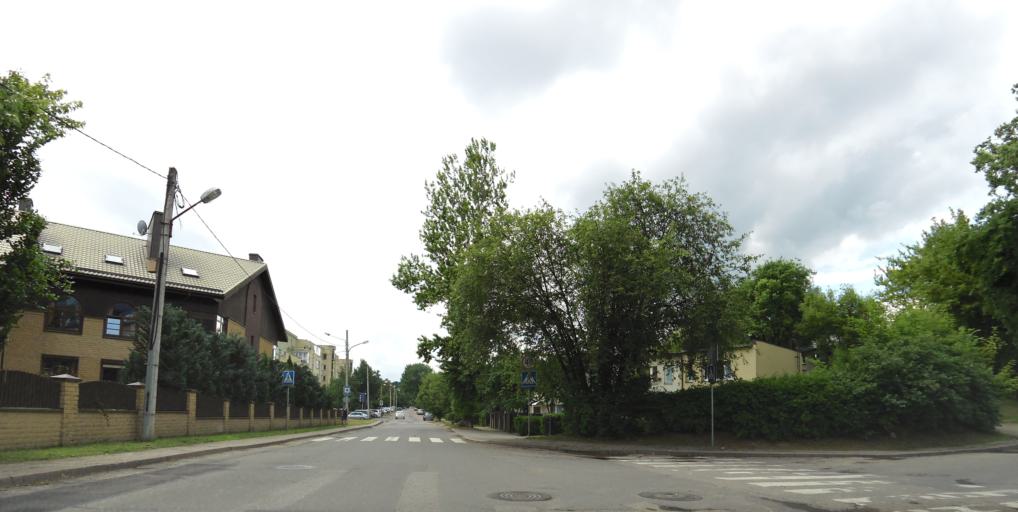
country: LT
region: Vilnius County
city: Seskine
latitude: 54.7020
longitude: 25.2510
